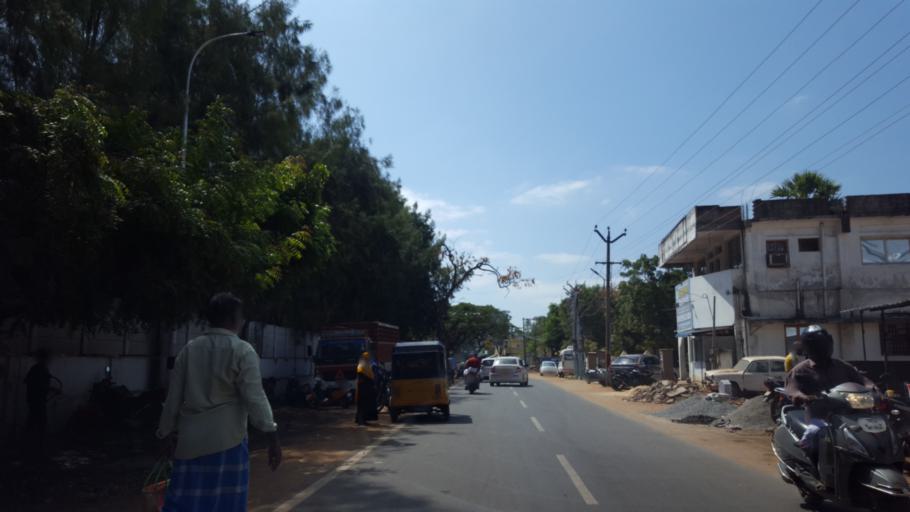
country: IN
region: Tamil Nadu
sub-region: Kancheepuram
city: Mamallapuram
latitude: 12.6239
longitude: 80.1942
